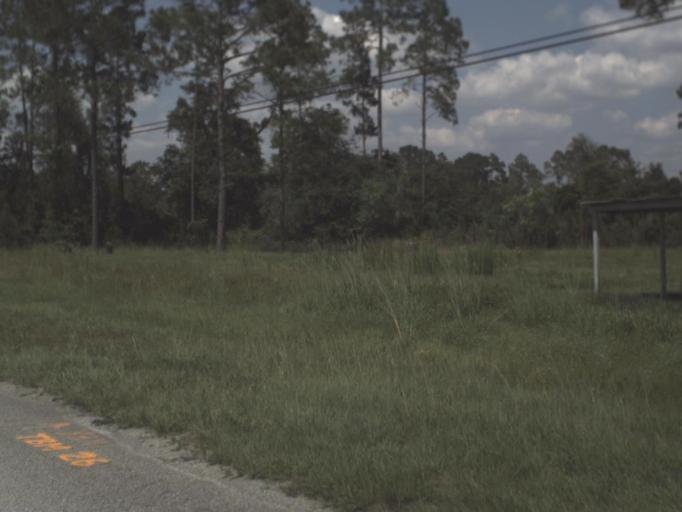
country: US
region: Florida
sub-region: Alachua County
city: Hawthorne
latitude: 29.5655
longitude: -82.0936
